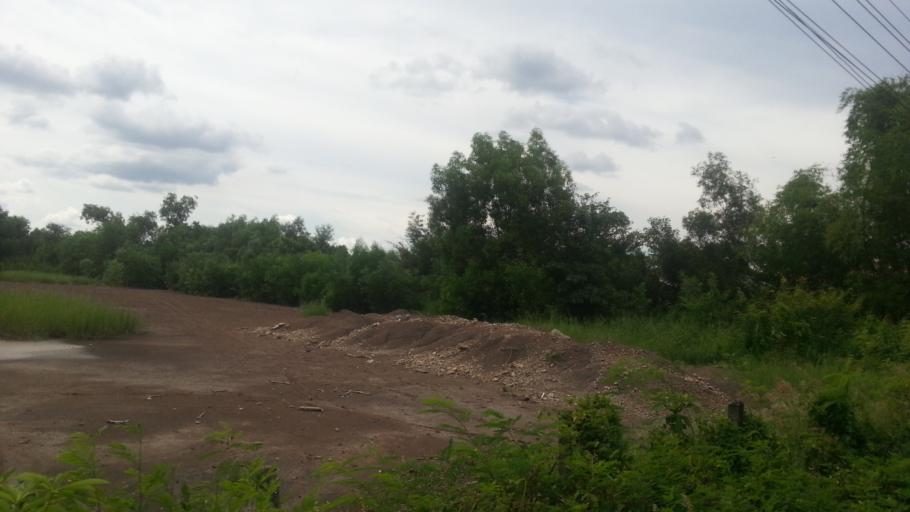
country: TH
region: Pathum Thani
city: Nong Suea
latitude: 14.1551
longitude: 100.8232
